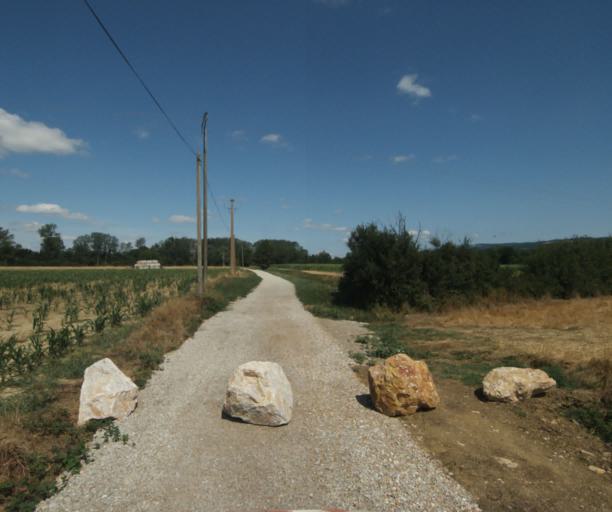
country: FR
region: Midi-Pyrenees
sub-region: Departement de la Haute-Garonne
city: Revel
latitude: 43.4592
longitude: 2.0257
